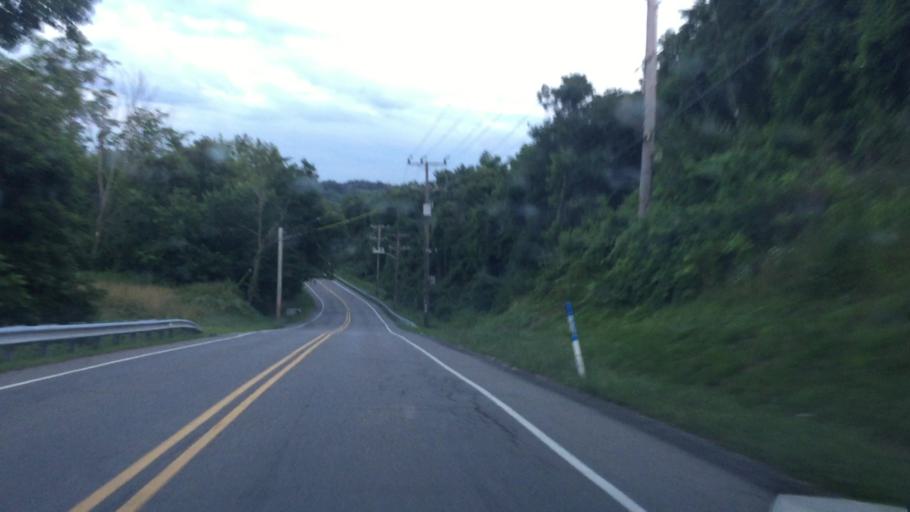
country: US
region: Pennsylvania
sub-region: Allegheny County
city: Rennerdale
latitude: 40.4415
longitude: -80.1469
